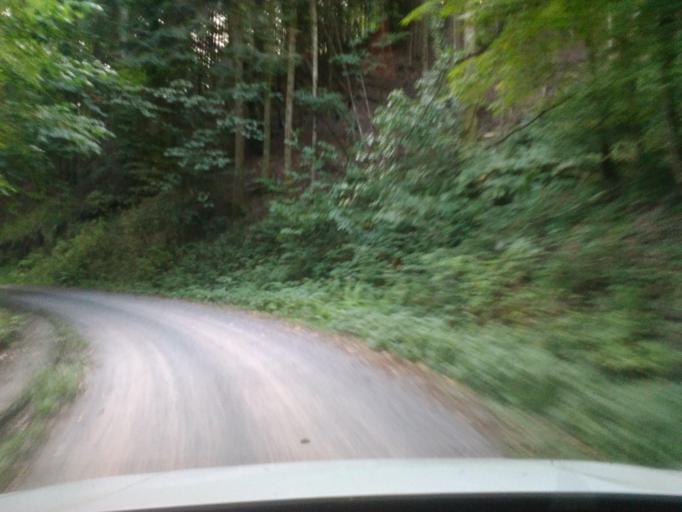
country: FR
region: Lorraine
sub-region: Departement des Vosges
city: Senones
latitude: 48.4062
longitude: 6.9762
